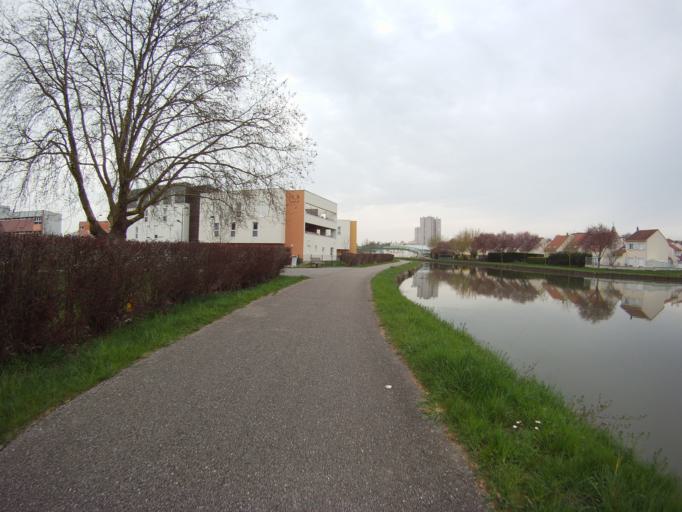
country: FR
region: Lorraine
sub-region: Departement de Meurthe-et-Moselle
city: Jarville-la-Malgrange
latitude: 48.6713
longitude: 6.2079
